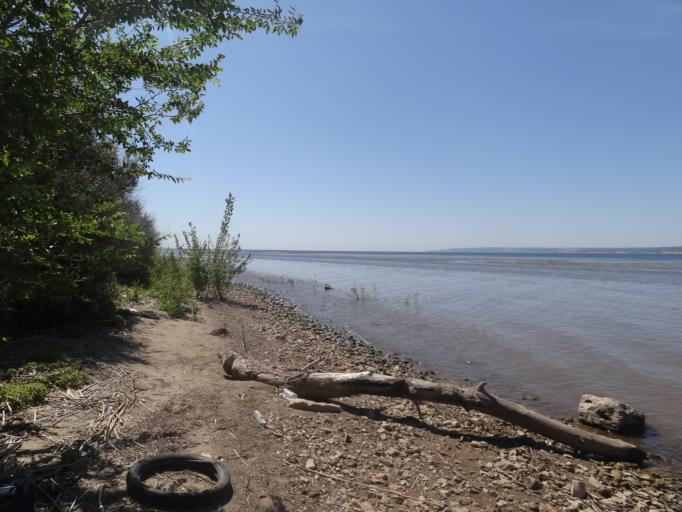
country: RU
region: Saratov
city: Krasnoarmeysk
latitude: 51.0779
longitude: 45.9538
